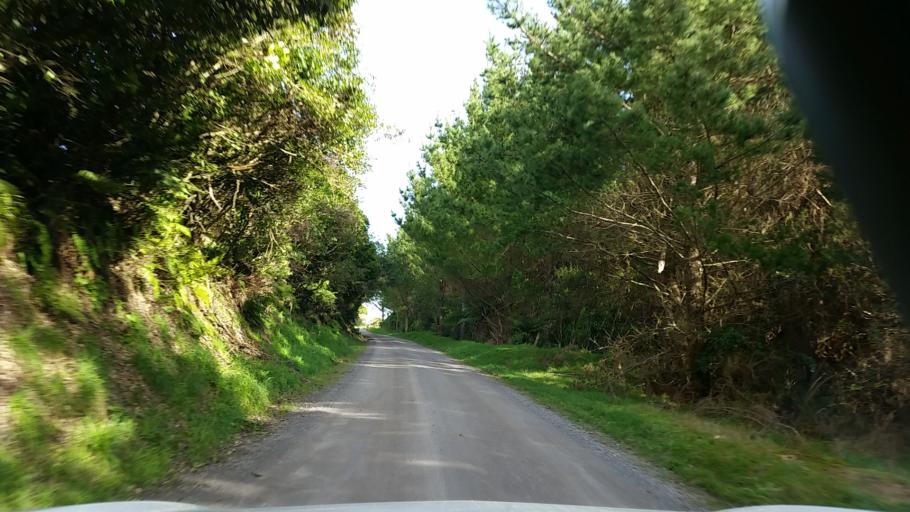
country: NZ
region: Bay of Plenty
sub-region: Rotorua District
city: Rotorua
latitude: -38.2396
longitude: 176.3484
